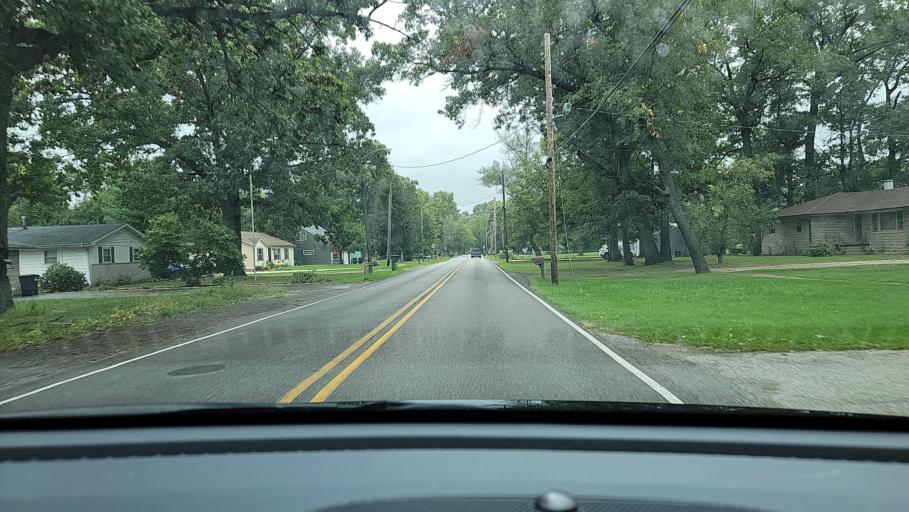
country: US
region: Indiana
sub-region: Lake County
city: Lake Station
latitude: 41.5664
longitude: -87.2218
